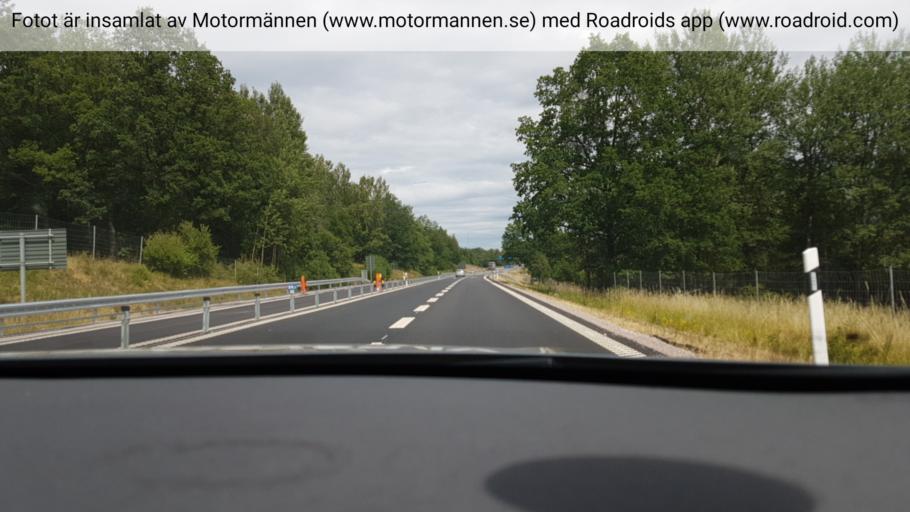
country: SE
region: Joenkoeping
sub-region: Tranas Kommun
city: Tranas
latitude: 58.0172
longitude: 14.9384
